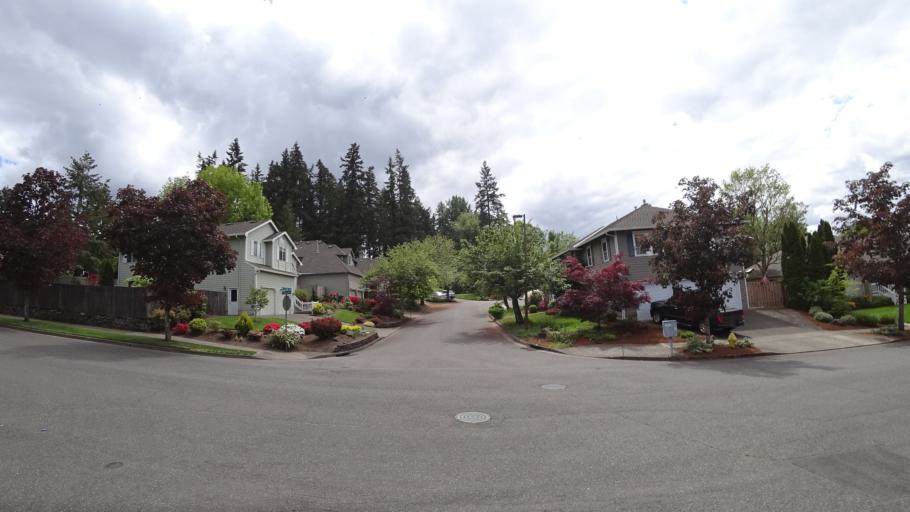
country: US
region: Oregon
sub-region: Washington County
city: Aloha
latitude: 45.4704
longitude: -122.8486
